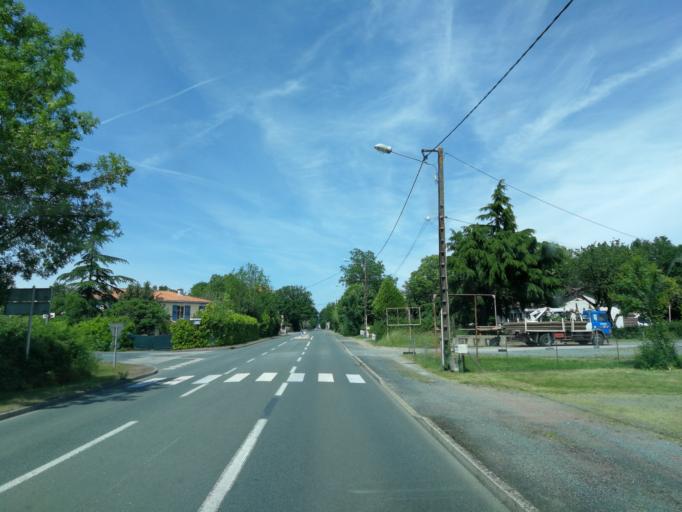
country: FR
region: Pays de la Loire
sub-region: Departement de la Vendee
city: Pissotte
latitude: 46.5295
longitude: -0.8075
